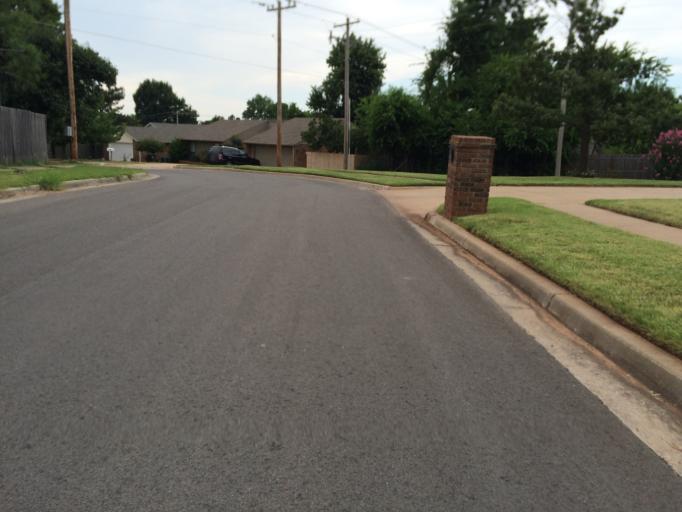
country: US
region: Oklahoma
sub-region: Cleveland County
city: Hall Park
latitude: 35.2543
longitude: -97.4321
